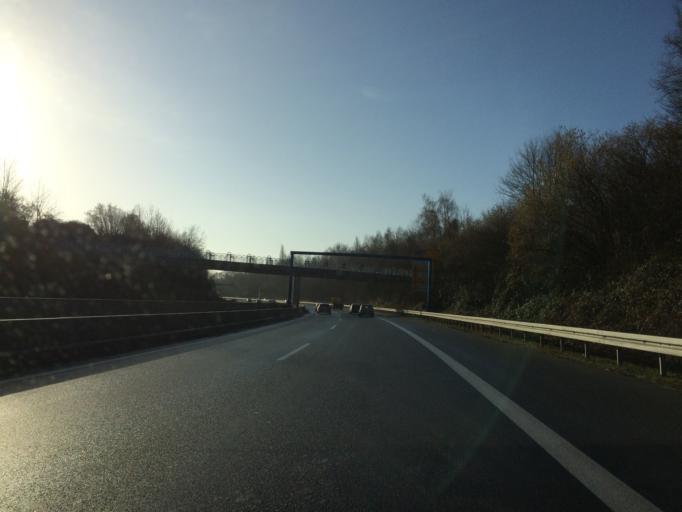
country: DE
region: North Rhine-Westphalia
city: Bochum-Hordel
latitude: 51.4747
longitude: 7.1870
